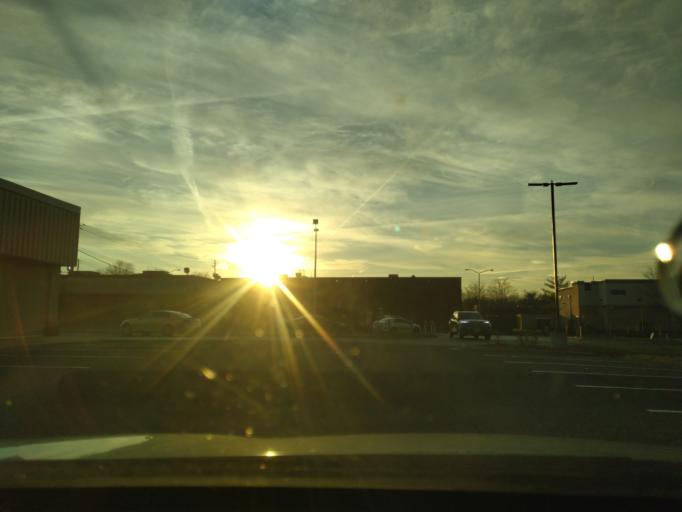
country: US
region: Maryland
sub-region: Prince George's County
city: Clinton
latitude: 38.7681
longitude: -76.8870
